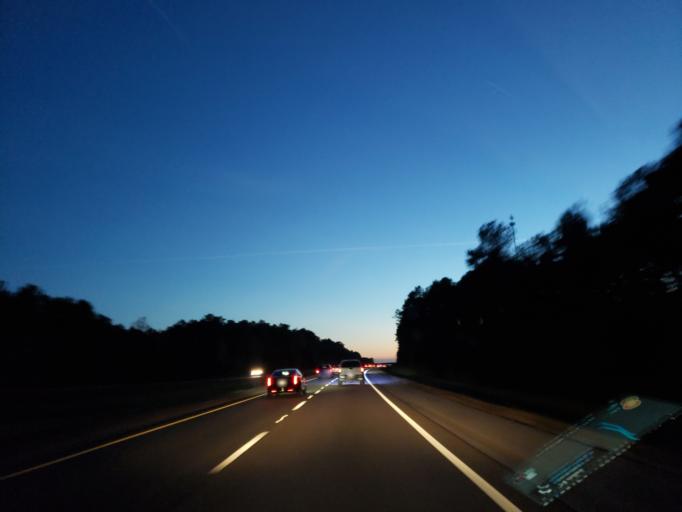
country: US
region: Mississippi
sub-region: Clarke County
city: Stonewall
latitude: 32.2496
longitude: -88.8254
